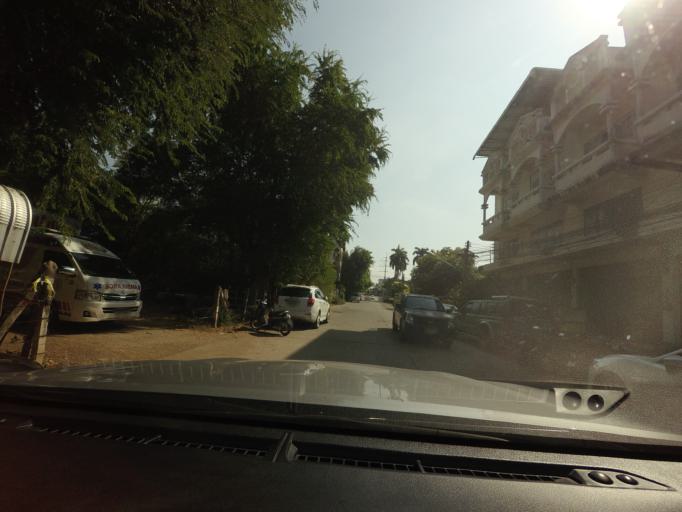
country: TH
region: Lampang
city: Lampang
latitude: 18.2795
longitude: 99.4858
